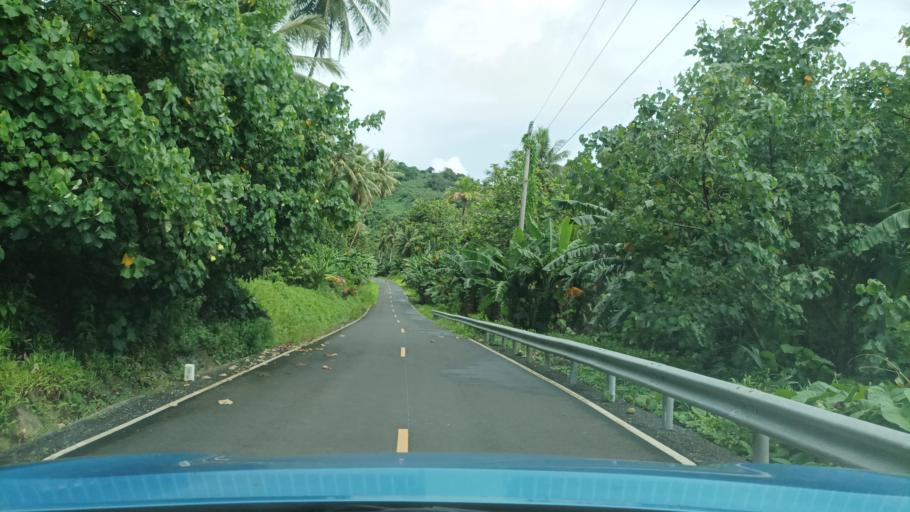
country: FM
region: Pohnpei
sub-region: Madolenihm Municipality
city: Madolenihm Municipality Government
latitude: 6.8665
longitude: 158.3292
